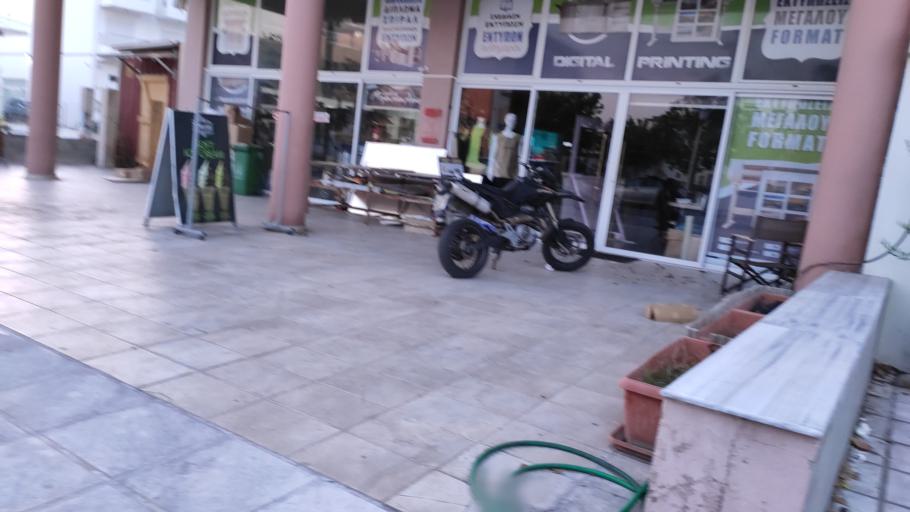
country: GR
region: South Aegean
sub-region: Nomos Dodekanisou
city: Kos
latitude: 36.9020
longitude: 27.2831
